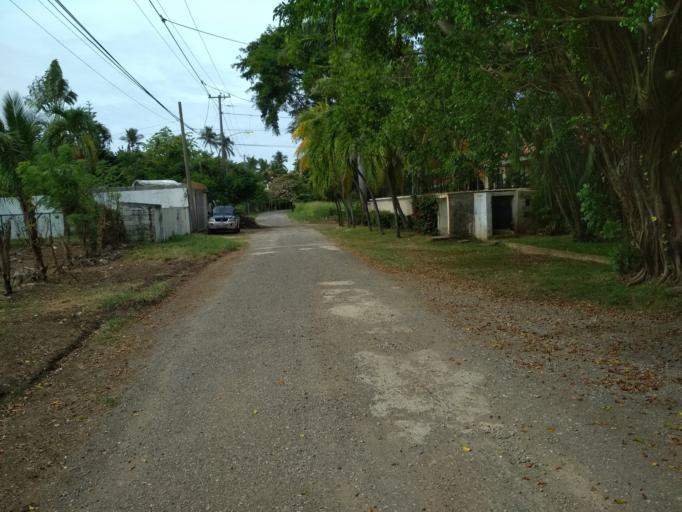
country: DO
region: Puerto Plata
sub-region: Puerto Plata
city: Puerto Plata
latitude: 19.8067
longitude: -70.7048
